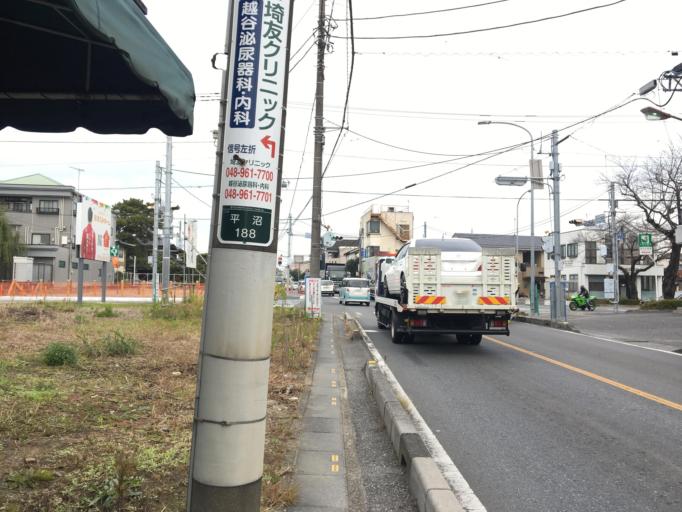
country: JP
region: Saitama
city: Yoshikawa
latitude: 35.8853
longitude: 139.8414
